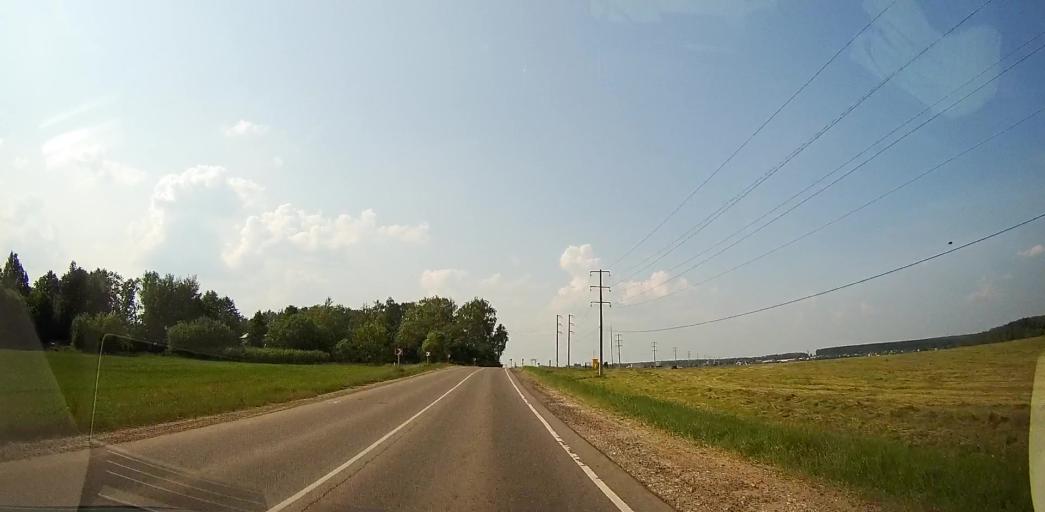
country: RU
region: Moskovskaya
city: Barybino
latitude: 55.2625
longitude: 37.9186
